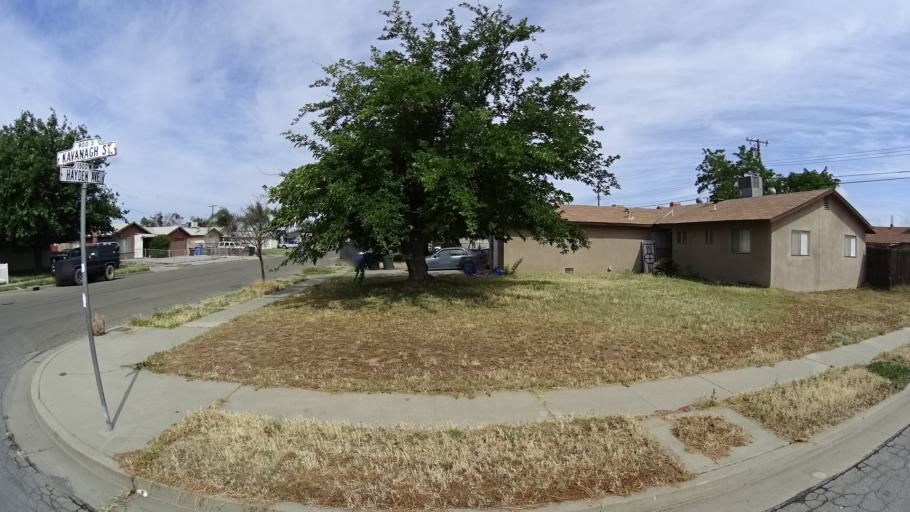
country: US
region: California
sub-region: Kings County
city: Hanford
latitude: 36.3153
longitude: -119.6686
